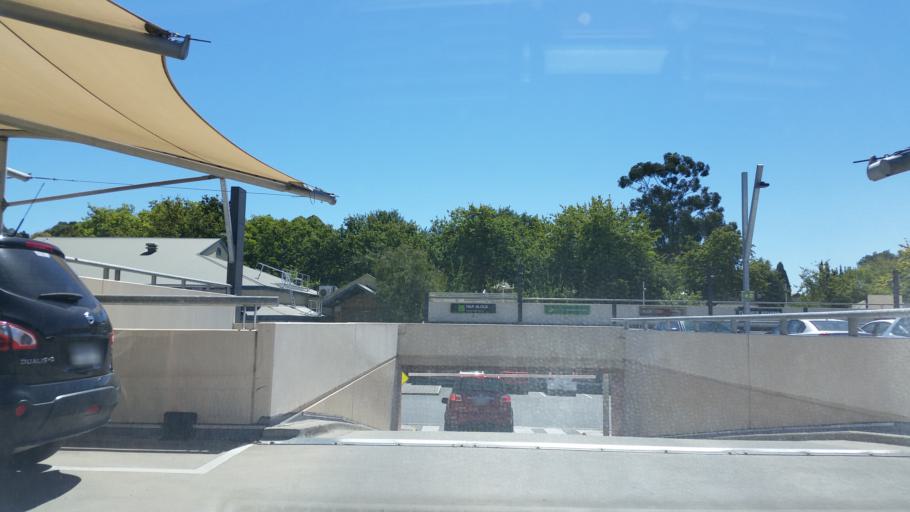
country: AU
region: South Australia
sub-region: Mount Barker
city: Mount Barker
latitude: -35.0645
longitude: 138.8591
